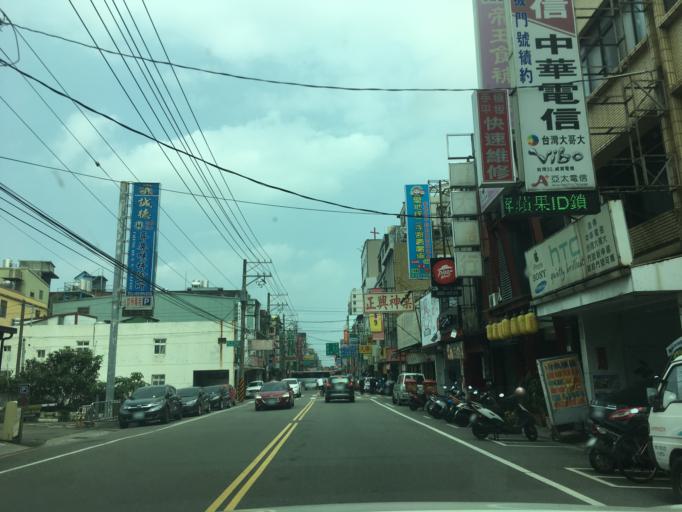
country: TW
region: Taiwan
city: Daxi
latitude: 24.8796
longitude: 121.2885
